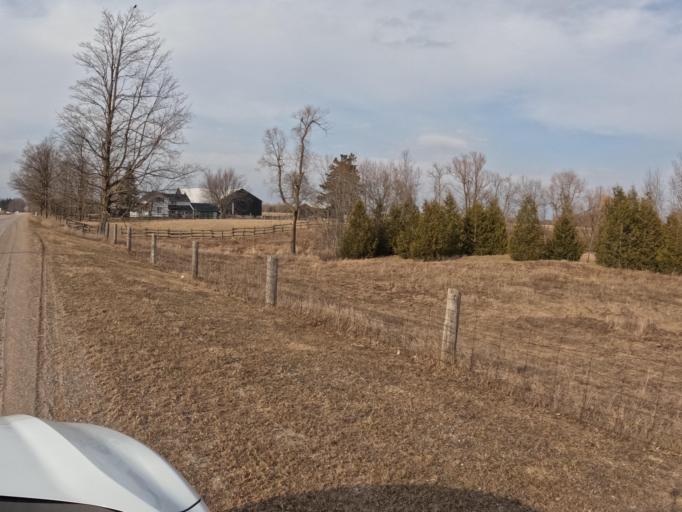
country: CA
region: Ontario
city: Orangeville
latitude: 43.8907
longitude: -80.2655
